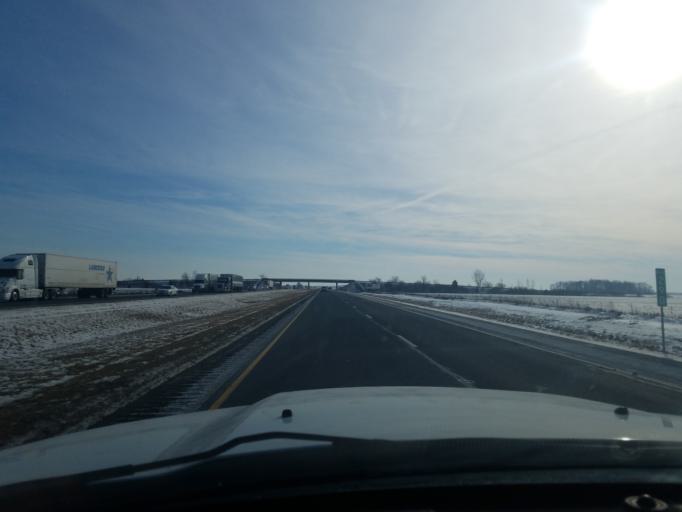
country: US
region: Indiana
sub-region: Huntington County
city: Markle
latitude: 40.8778
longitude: -85.3454
